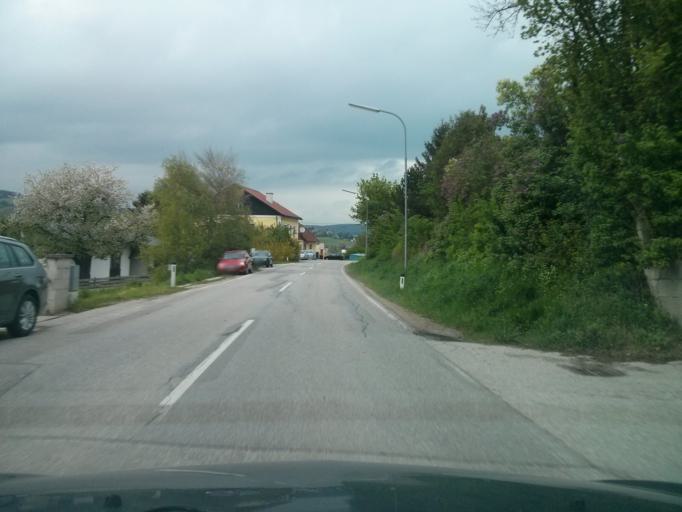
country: AT
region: Lower Austria
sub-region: Politischer Bezirk Baden
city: Berndorf
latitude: 47.9268
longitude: 16.0949
